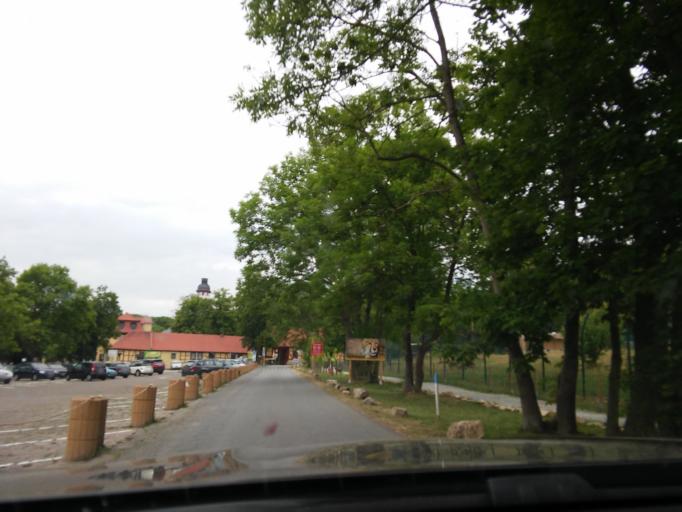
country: DE
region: Thuringia
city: Sondershausen
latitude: 51.3382
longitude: 10.8632
